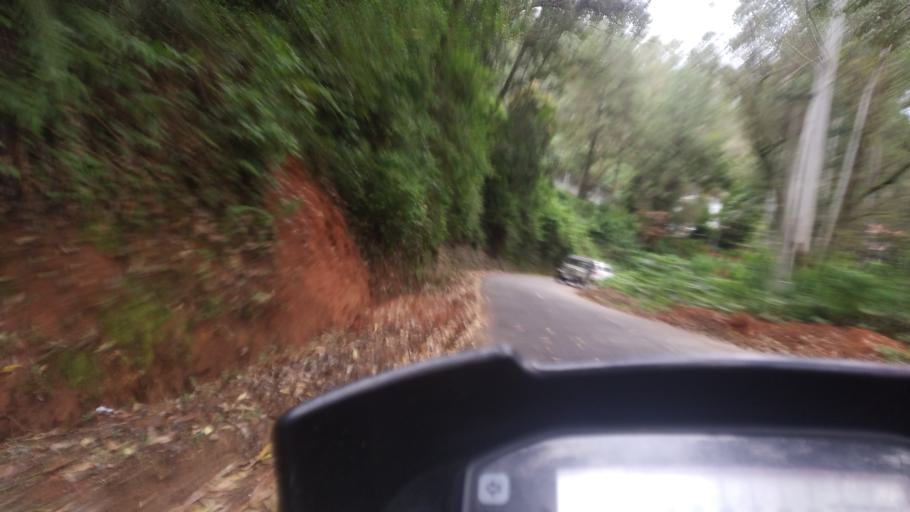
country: IN
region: Kerala
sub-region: Idukki
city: Munnar
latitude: 10.0661
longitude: 77.1049
